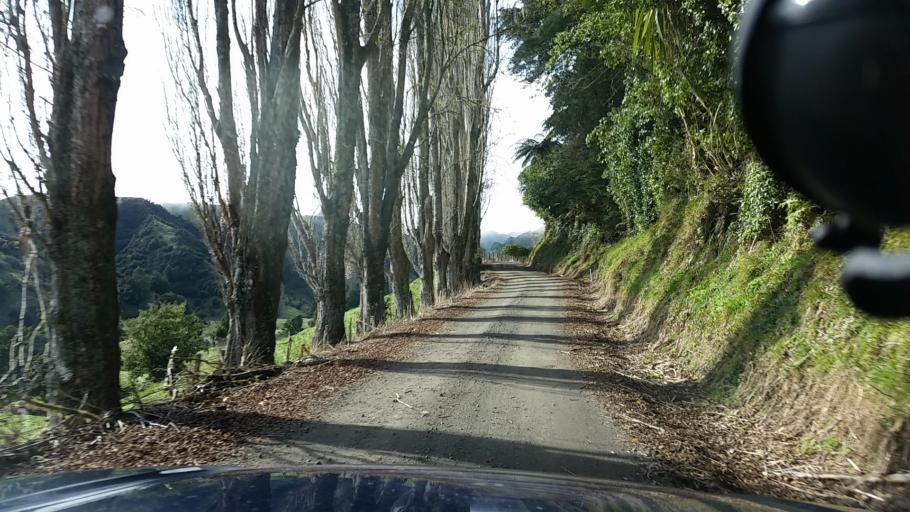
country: NZ
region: Taranaki
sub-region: New Plymouth District
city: Waitara
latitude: -39.0320
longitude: 174.7895
